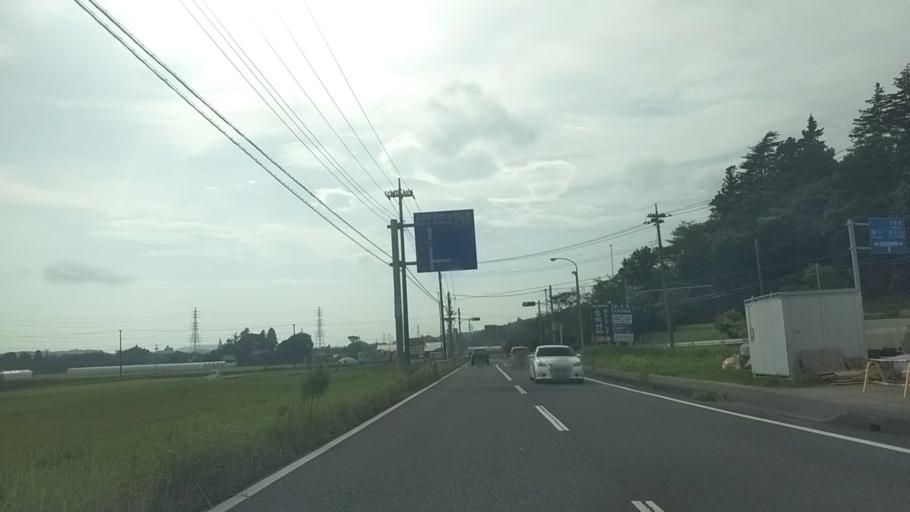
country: JP
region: Chiba
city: Kisarazu
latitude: 35.3100
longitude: 139.9706
